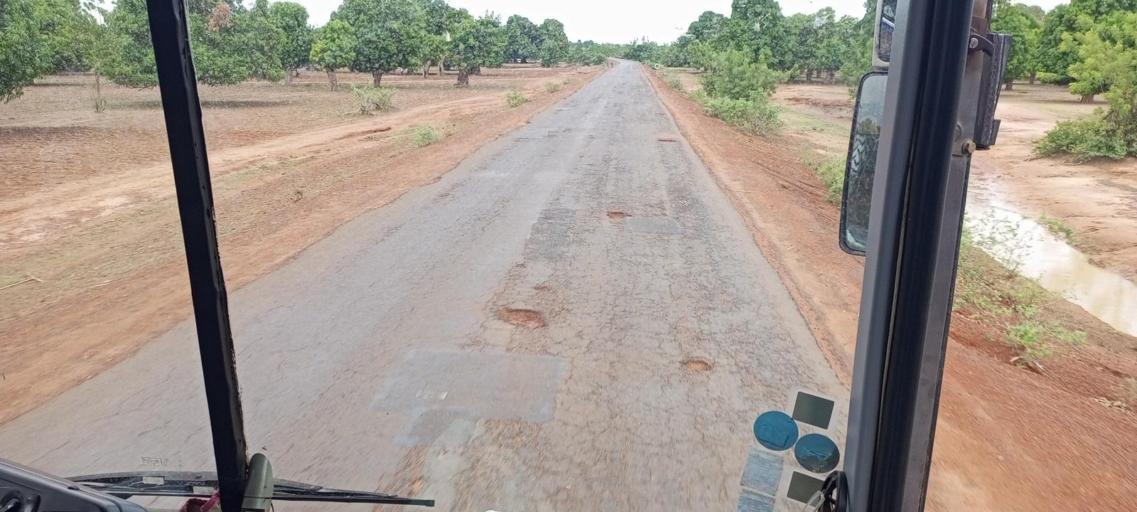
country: ML
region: Segou
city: Bla
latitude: 12.6820
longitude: -5.7235
